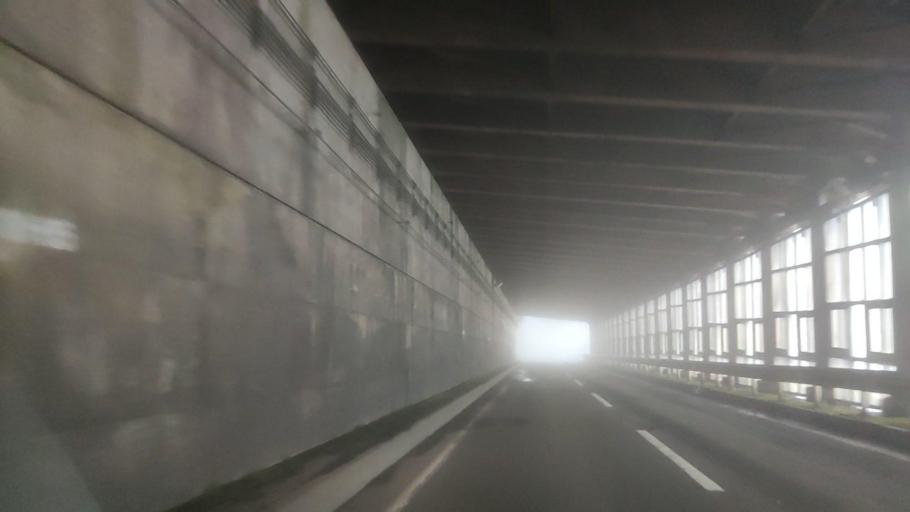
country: JP
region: Hokkaido
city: Date
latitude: 42.5511
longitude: 141.0826
